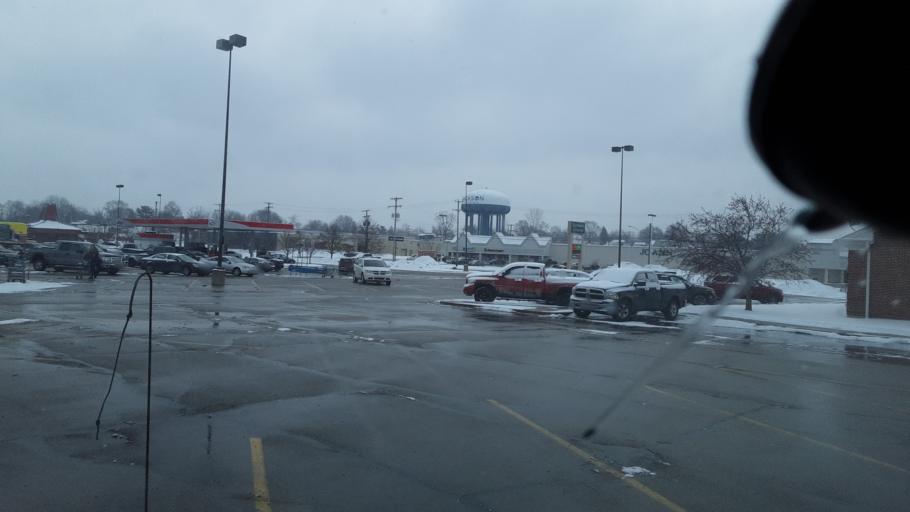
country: US
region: Michigan
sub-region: Jackson County
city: Jackson
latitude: 42.2630
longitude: -84.4276
